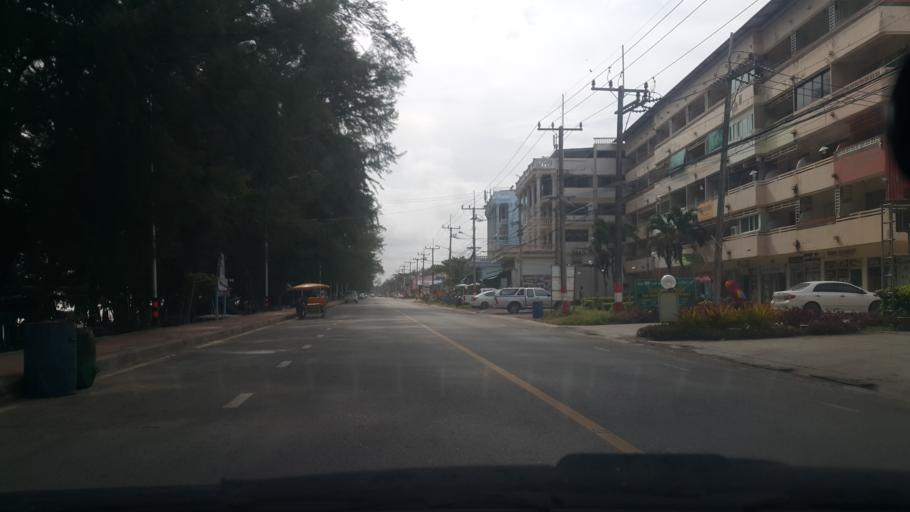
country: TH
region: Rayong
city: Rayong
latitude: 12.6135
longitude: 101.3808
